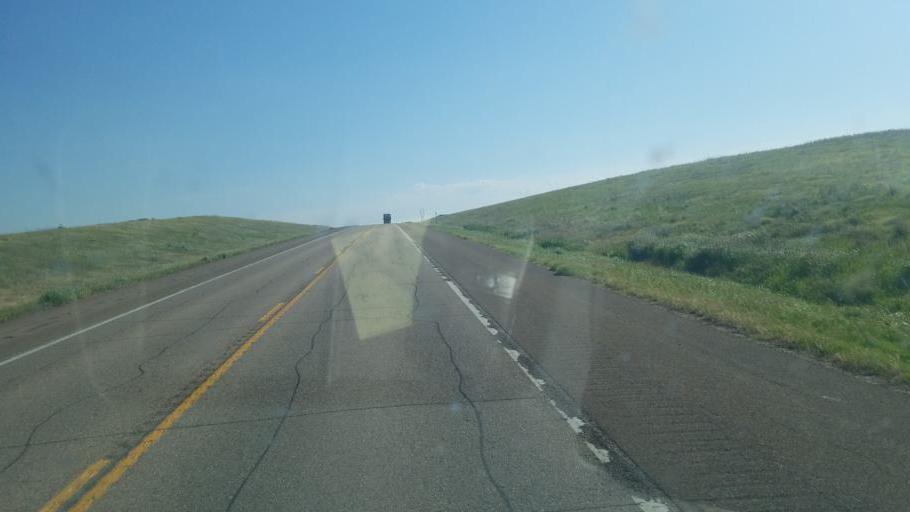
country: US
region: Kansas
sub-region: Barton County
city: Great Bend
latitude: 38.3842
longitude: -98.6815
